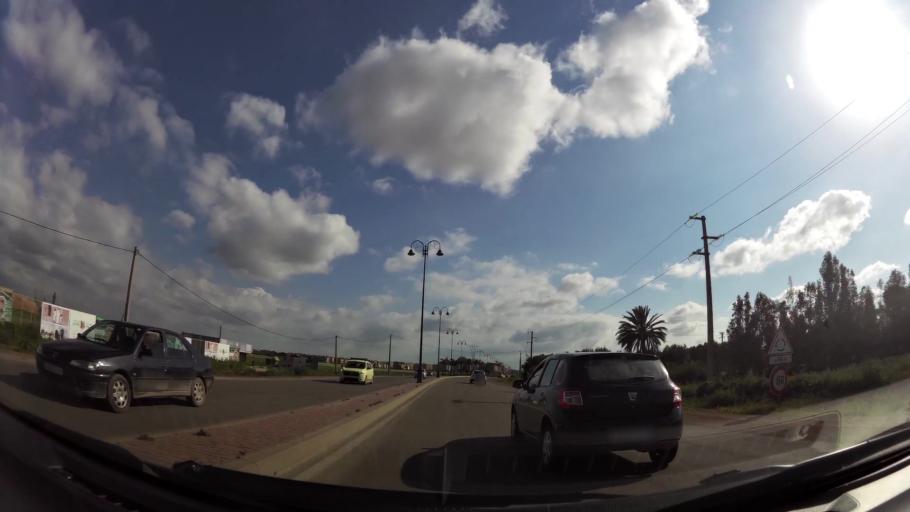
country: MA
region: Chaouia-Ouardigha
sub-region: Settat Province
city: Berrechid
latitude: 33.2861
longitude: -7.5778
